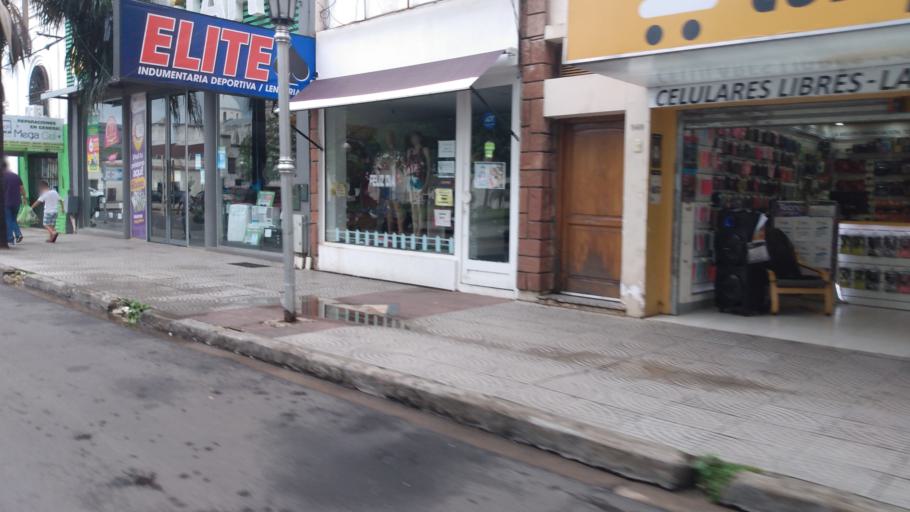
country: AR
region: Corrientes
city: Corrientes
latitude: -27.4684
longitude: -58.8320
